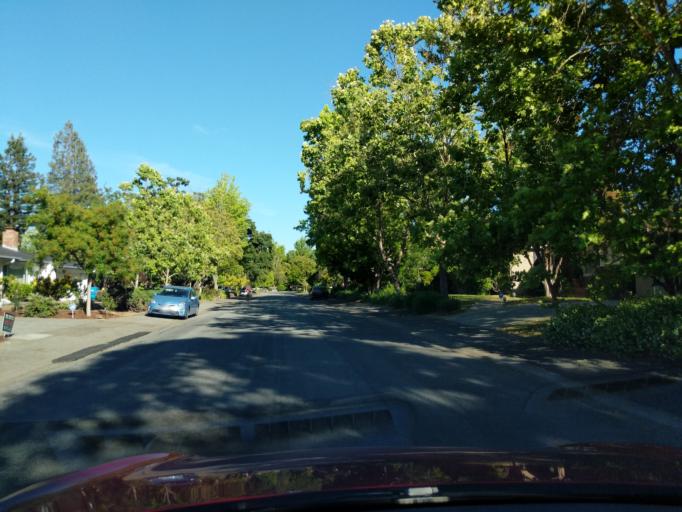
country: US
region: California
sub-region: San Mateo County
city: Menlo Park
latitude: 37.4433
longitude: -122.1872
